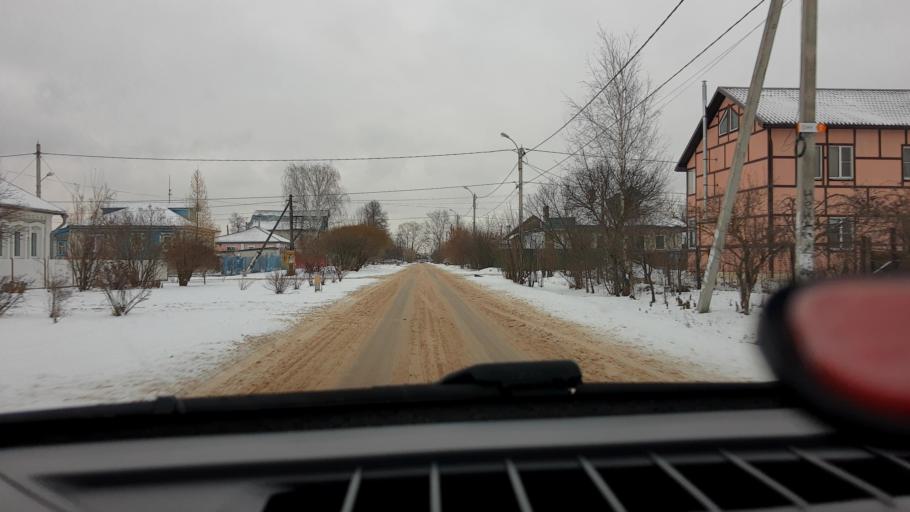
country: RU
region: Nizjnij Novgorod
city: Gorbatovka
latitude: 56.2684
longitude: 43.7668
